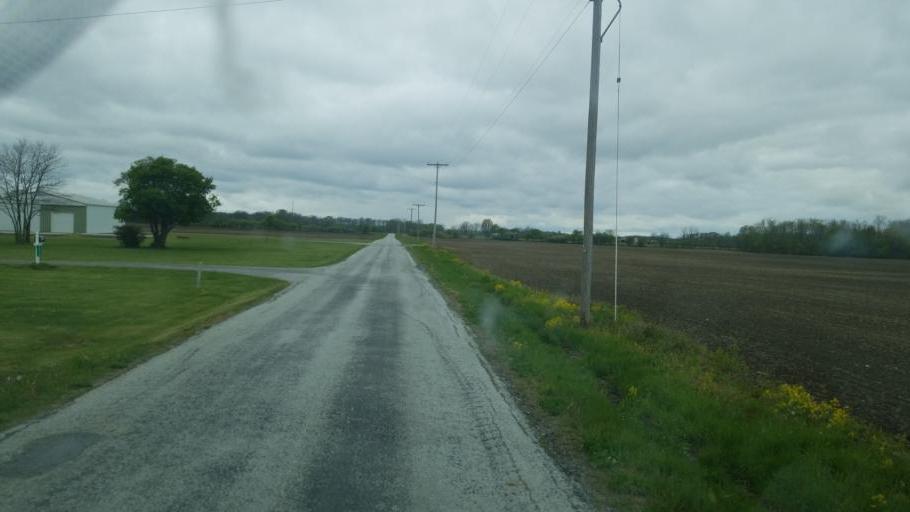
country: US
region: Ohio
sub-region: Hardin County
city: Kenton
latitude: 40.7245
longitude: -83.5799
